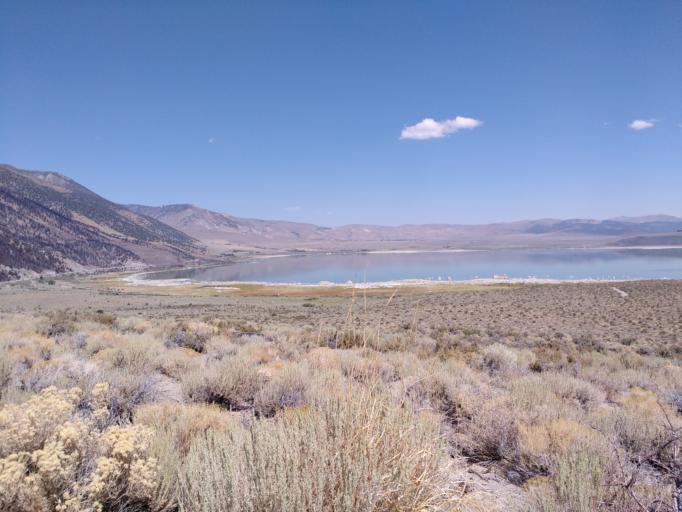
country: US
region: California
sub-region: Mono County
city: Bridgeport
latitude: 37.9673
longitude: -119.1200
